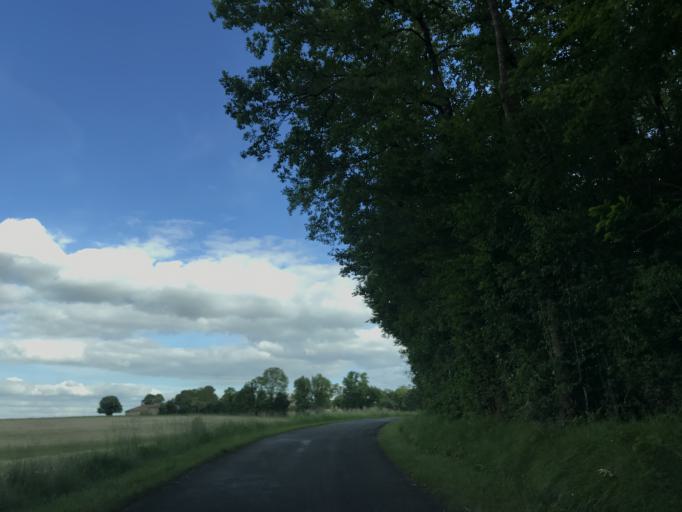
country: FR
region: Aquitaine
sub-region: Departement de la Dordogne
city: Saint-Aulaye
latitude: 45.2624
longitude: 0.1272
